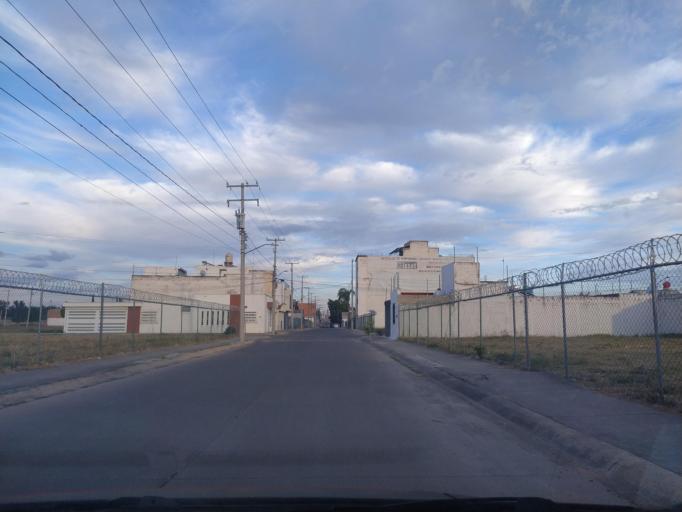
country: LA
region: Oudomxai
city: Muang La
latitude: 21.0188
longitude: 101.8688
